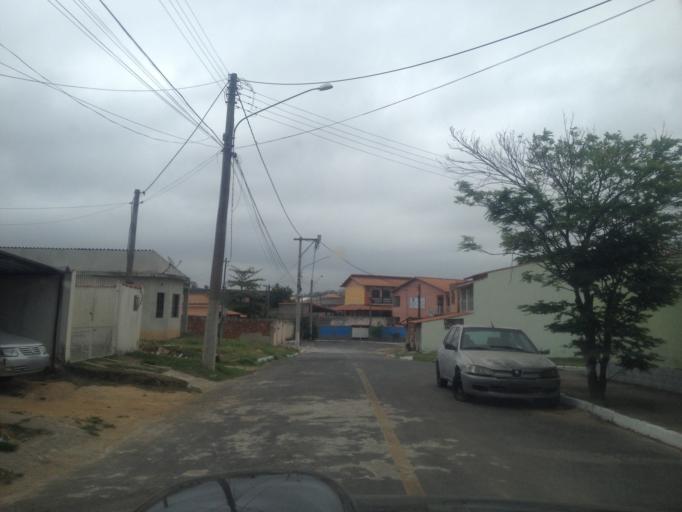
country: BR
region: Rio de Janeiro
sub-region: Porto Real
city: Porto Real
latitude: -22.4130
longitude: -44.3085
